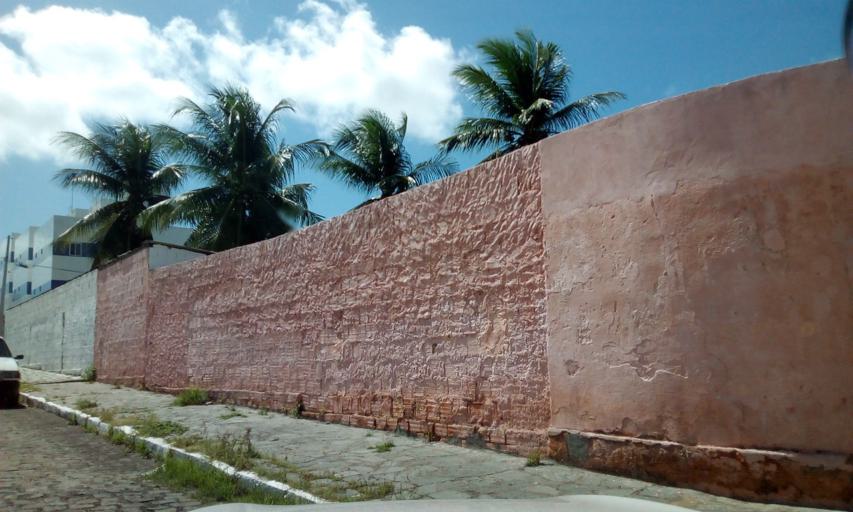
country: BR
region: Paraiba
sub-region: Joao Pessoa
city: Joao Pessoa
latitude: -7.1878
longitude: -34.8473
